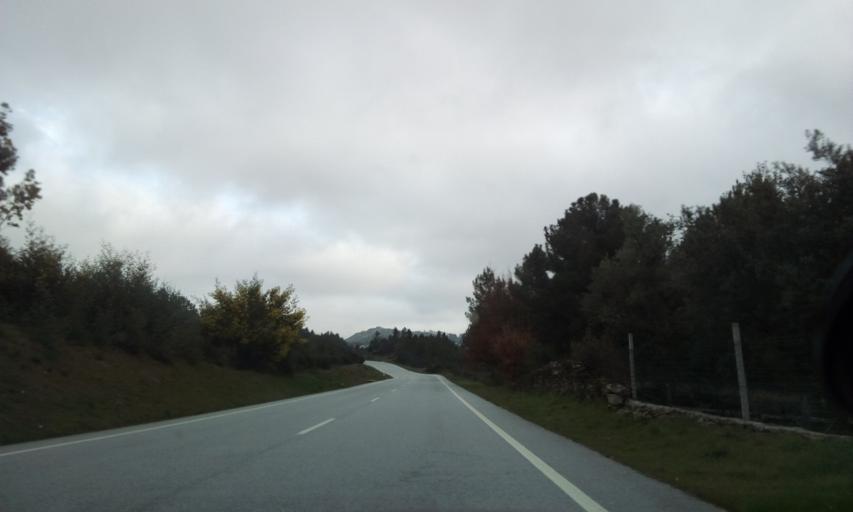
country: PT
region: Guarda
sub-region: Fornos de Algodres
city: Fornos de Algodres
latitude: 40.6428
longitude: -7.4927
